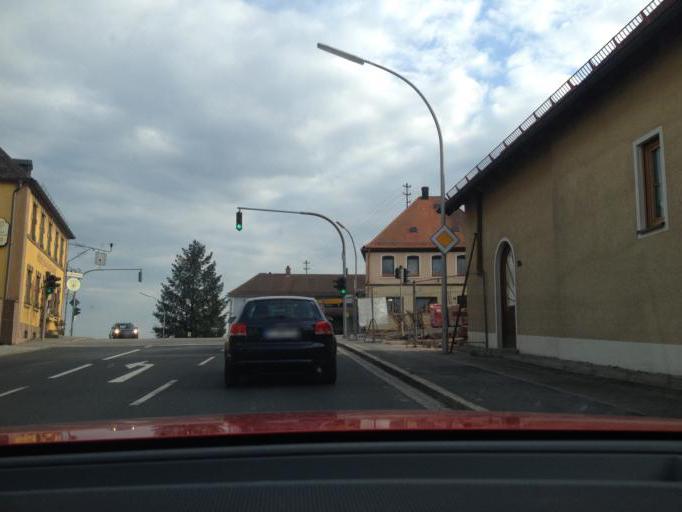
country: DE
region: Bavaria
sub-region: Upper Palatinate
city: Speinshart
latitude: 49.8267
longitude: 11.8391
